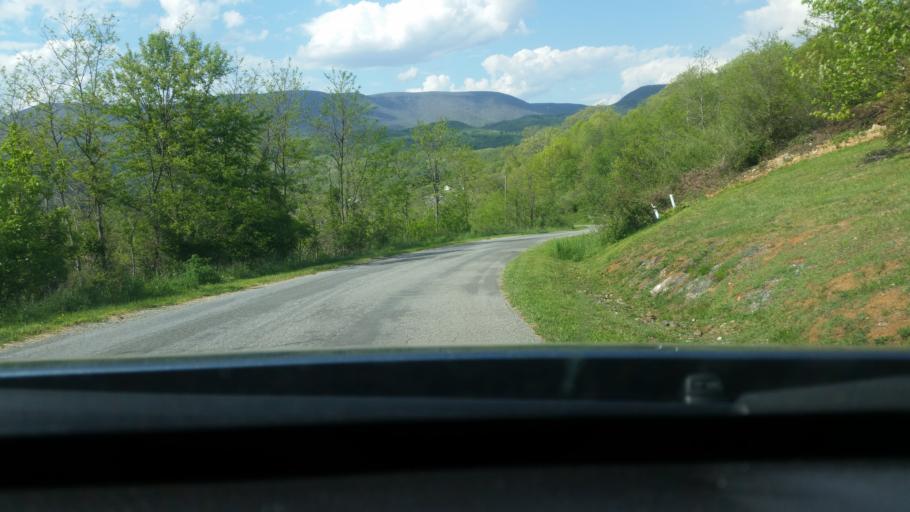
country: US
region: Virginia
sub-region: Giles County
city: Pembroke
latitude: 37.3076
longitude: -80.6337
